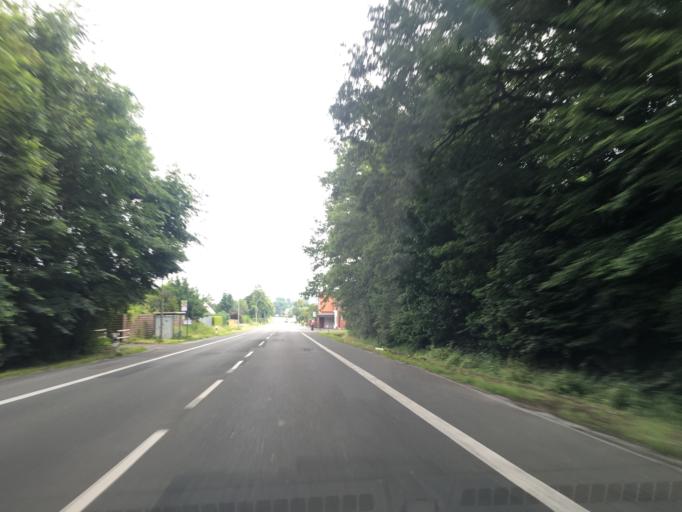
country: DE
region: North Rhine-Westphalia
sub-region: Regierungsbezirk Munster
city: Steinfurt
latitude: 52.1365
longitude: 7.4082
